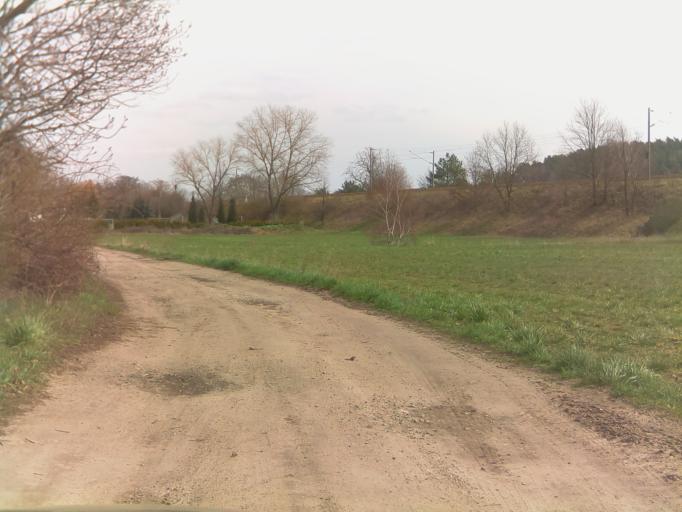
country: DE
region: Brandenburg
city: Bronkow
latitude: 51.6985
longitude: 13.8705
